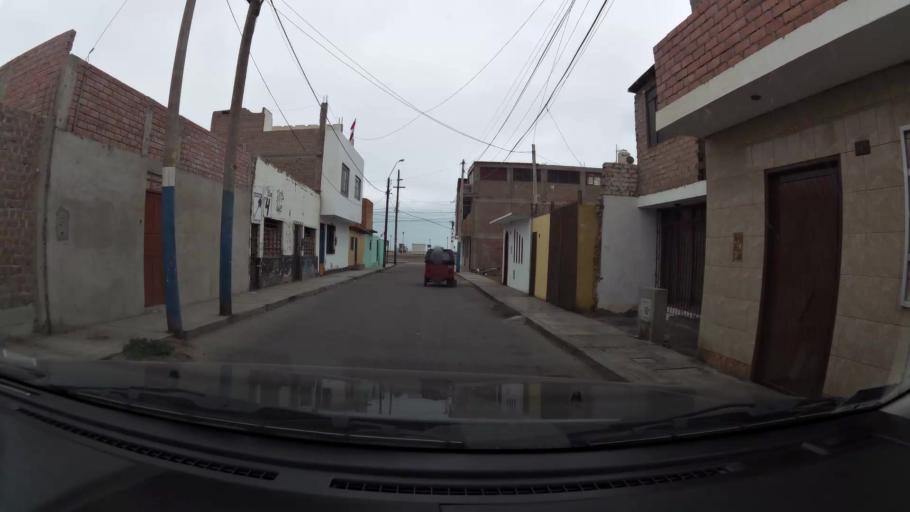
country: PE
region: Ica
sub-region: Provincia de Pisco
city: Pisco
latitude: -13.7086
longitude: -76.2174
